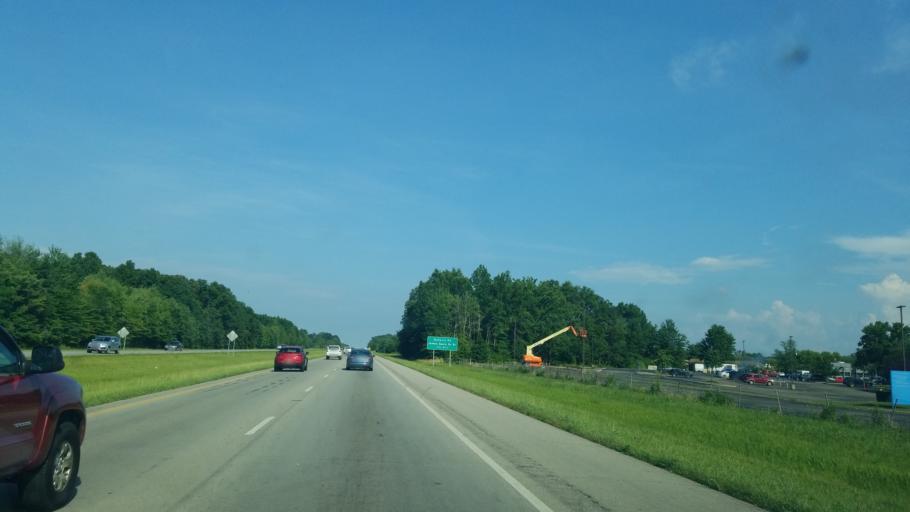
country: US
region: Ohio
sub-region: Clermont County
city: Batavia
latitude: 39.0818
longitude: -84.1450
